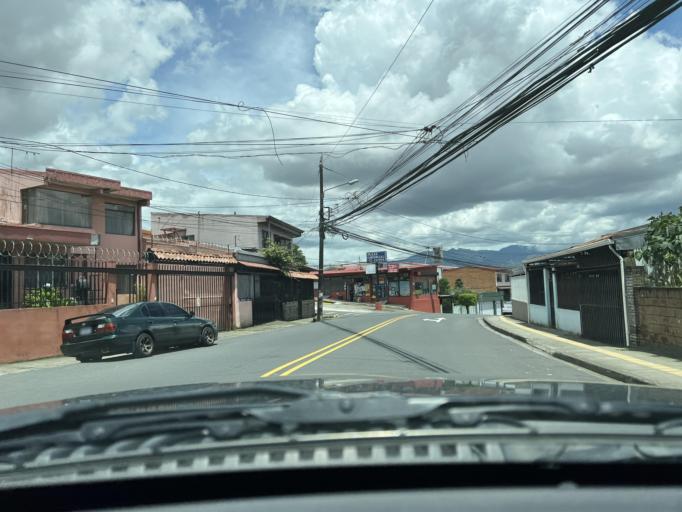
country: CR
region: San Jose
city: Sabanilla
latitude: 9.9405
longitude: -84.0280
